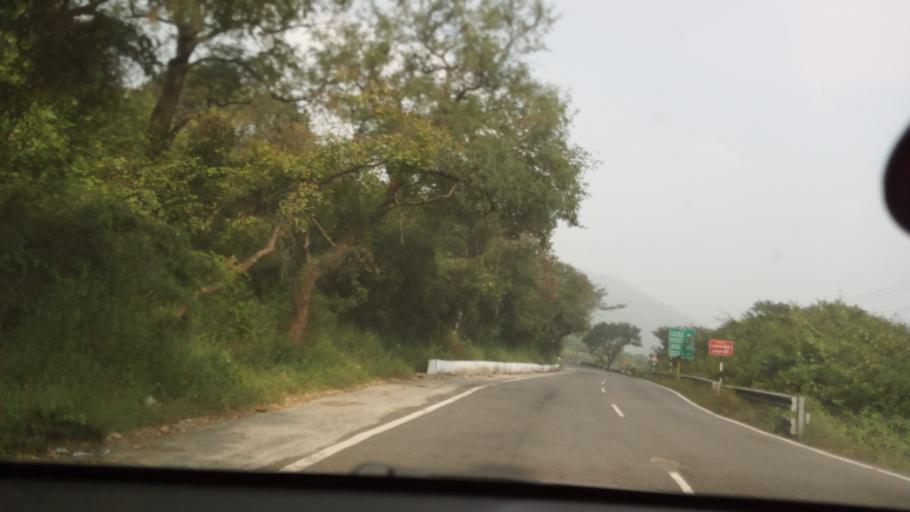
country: IN
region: Tamil Nadu
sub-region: Erode
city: Sathyamangalam
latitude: 11.5851
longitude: 77.1331
